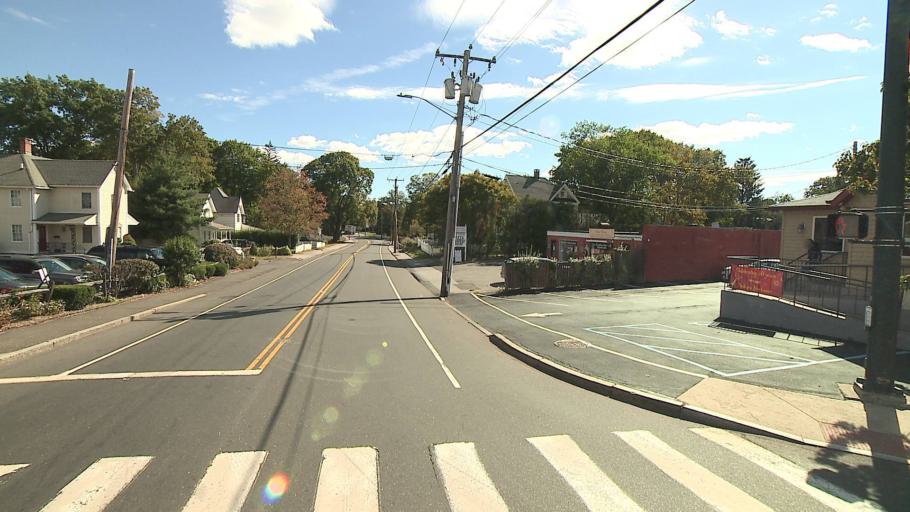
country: US
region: Connecticut
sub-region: Fairfield County
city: New Canaan
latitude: 41.1477
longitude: -73.4904
